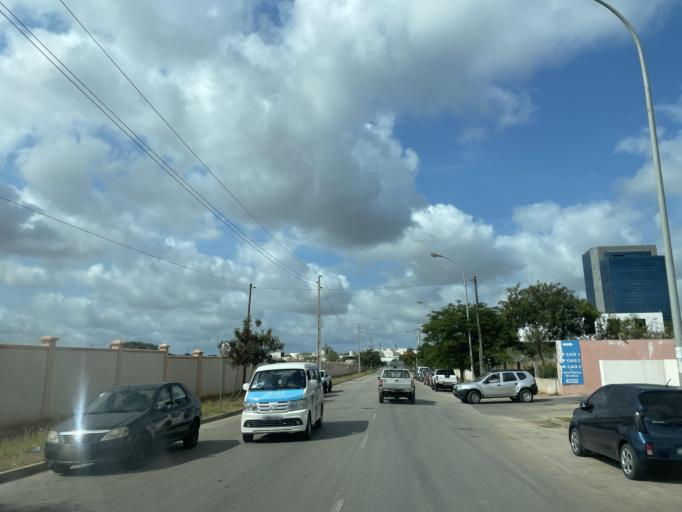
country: AO
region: Luanda
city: Luanda
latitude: -8.9289
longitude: 13.1918
